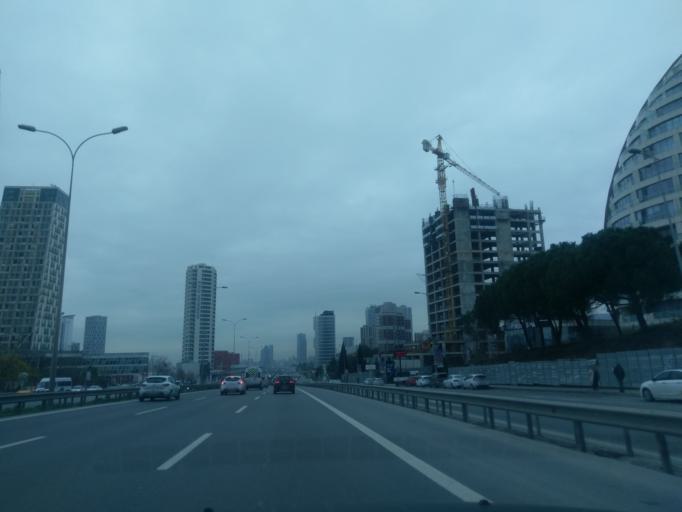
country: TR
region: Istanbul
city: Maltepe
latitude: 40.9095
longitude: 29.2023
